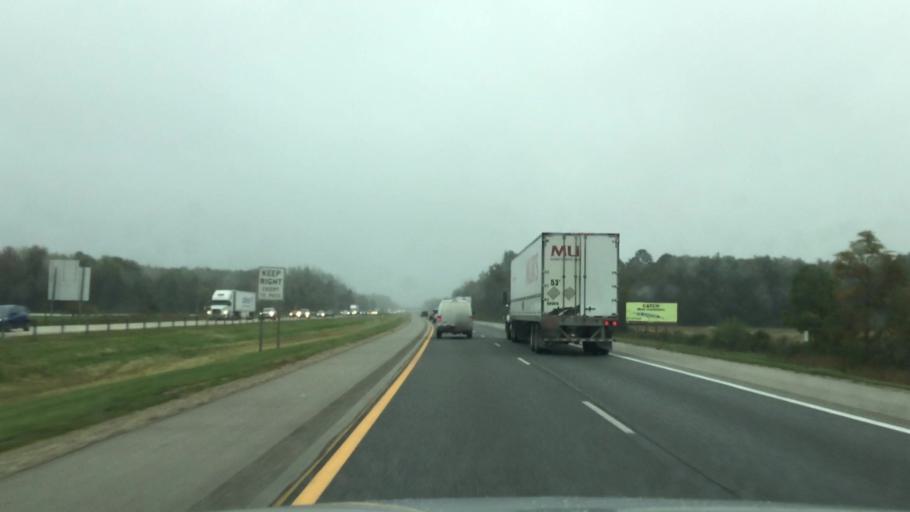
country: US
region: Michigan
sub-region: Berrien County
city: Watervliet
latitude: 42.1798
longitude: -86.2398
